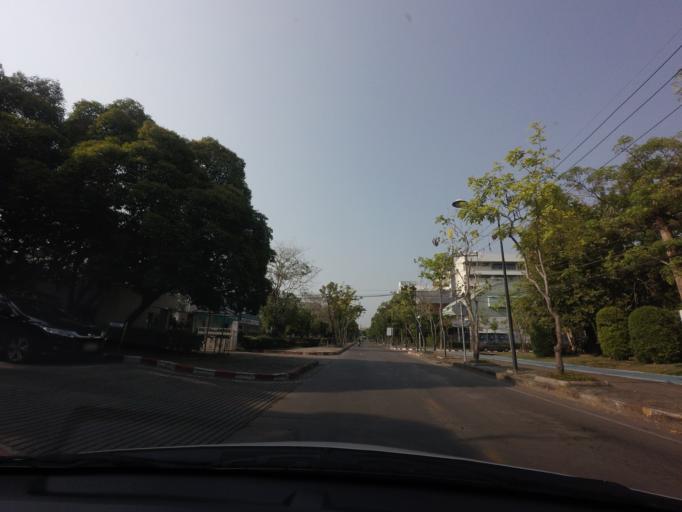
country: TH
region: Nakhon Pathom
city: Salaya
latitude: 13.7985
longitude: 100.3182
